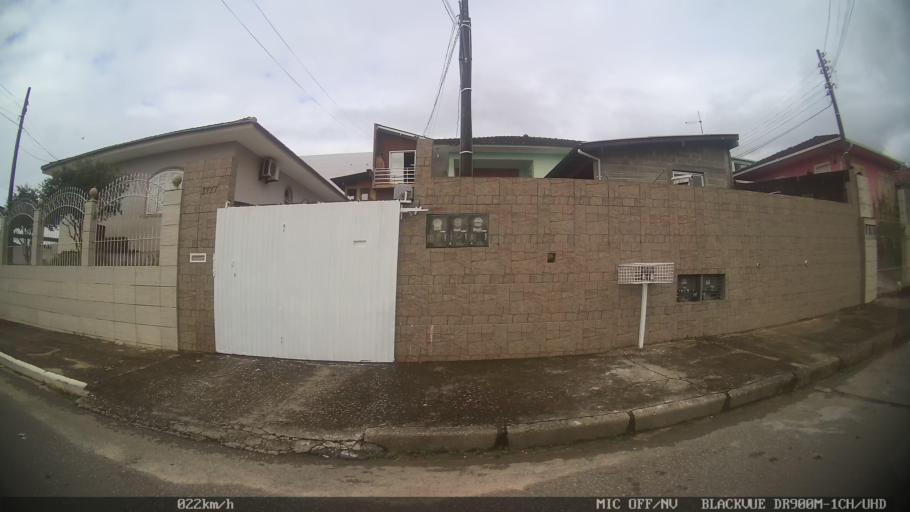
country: BR
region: Santa Catarina
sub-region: Sao Jose
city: Campinas
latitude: -27.5651
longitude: -48.6325
